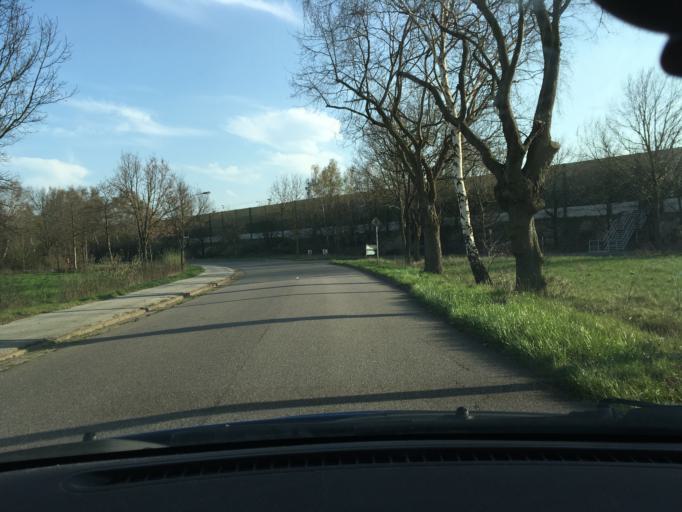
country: DE
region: Lower Saxony
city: Stelle
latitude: 53.4071
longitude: 10.0624
